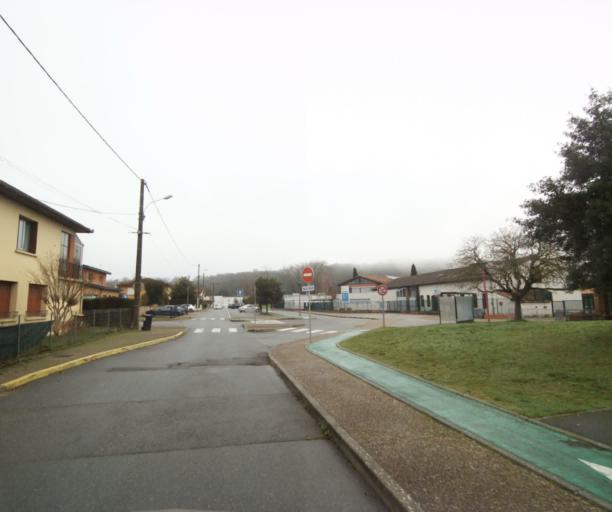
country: FR
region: Midi-Pyrenees
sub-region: Departement de la Haute-Garonne
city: Villemur-sur-Tarn
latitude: 43.8584
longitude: 1.5034
